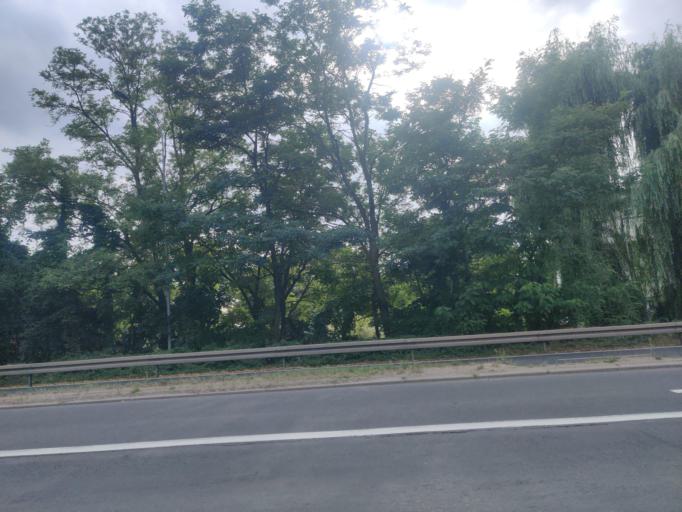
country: PL
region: Greater Poland Voivodeship
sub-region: Konin
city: Konin
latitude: 52.2172
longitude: 18.2543
